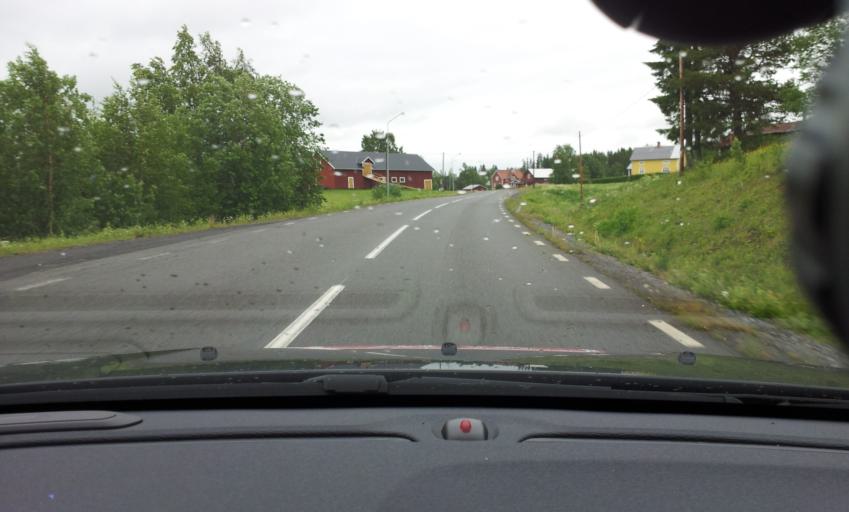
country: SE
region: Jaemtland
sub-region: OEstersunds Kommun
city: Lit
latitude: 63.6799
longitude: 15.0438
